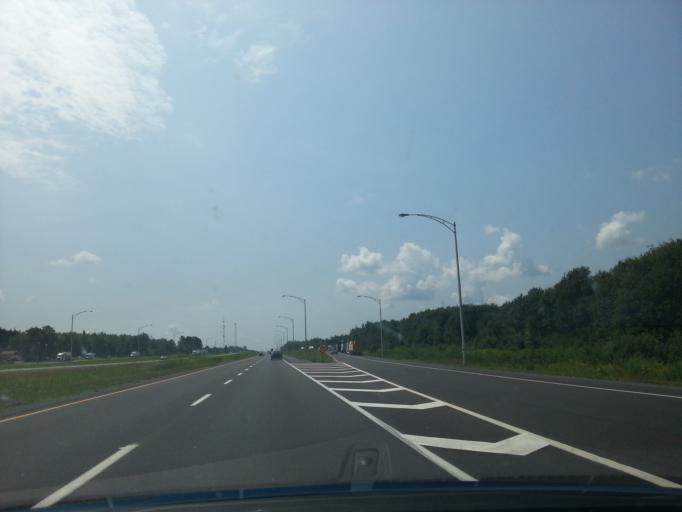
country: CA
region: Quebec
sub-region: Mauricie
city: Plessisville
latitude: 46.3909
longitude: -71.8389
